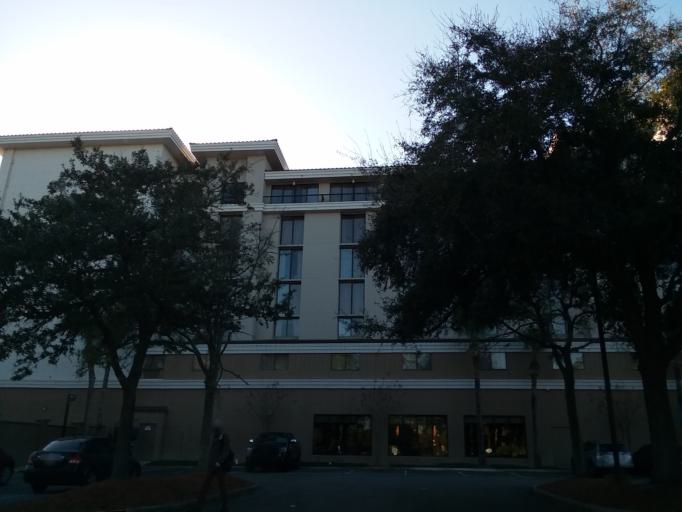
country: US
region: Florida
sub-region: Saint Johns County
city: Fruit Cove
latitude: 30.2201
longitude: -81.5645
